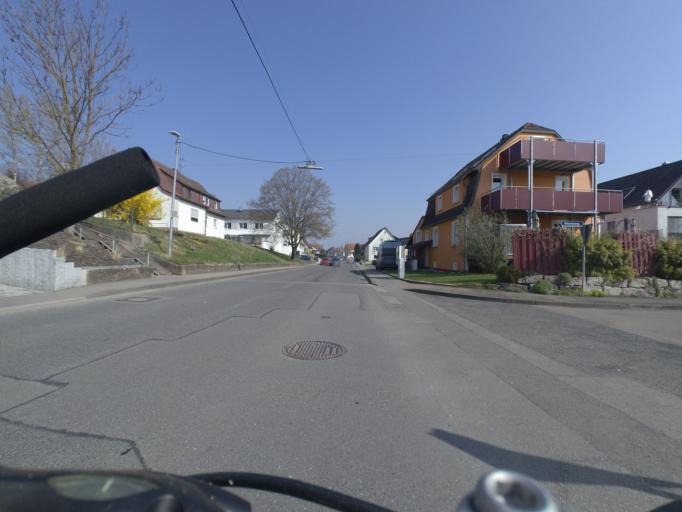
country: DE
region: Baden-Wuerttemberg
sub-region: Regierungsbezirk Stuttgart
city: Unterensingen
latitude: 48.6536
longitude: 9.3534
